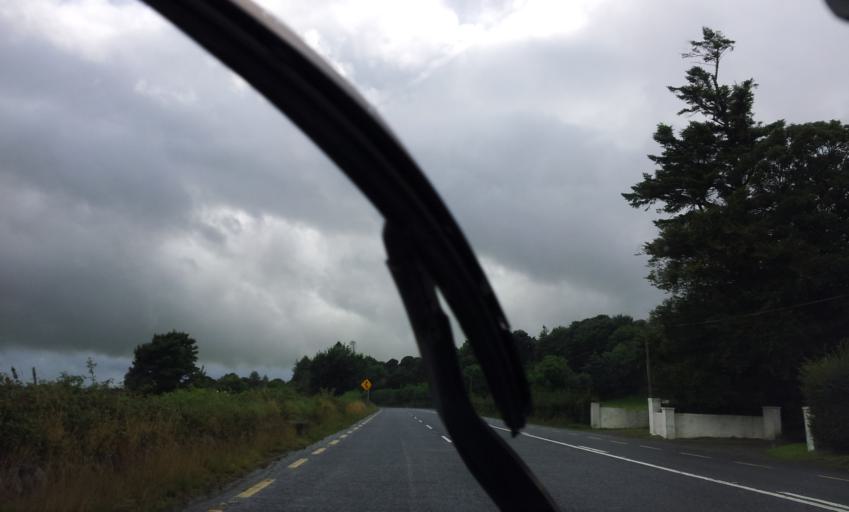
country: IE
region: Munster
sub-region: Waterford
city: Dungarvan
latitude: 52.1504
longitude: -7.5382
